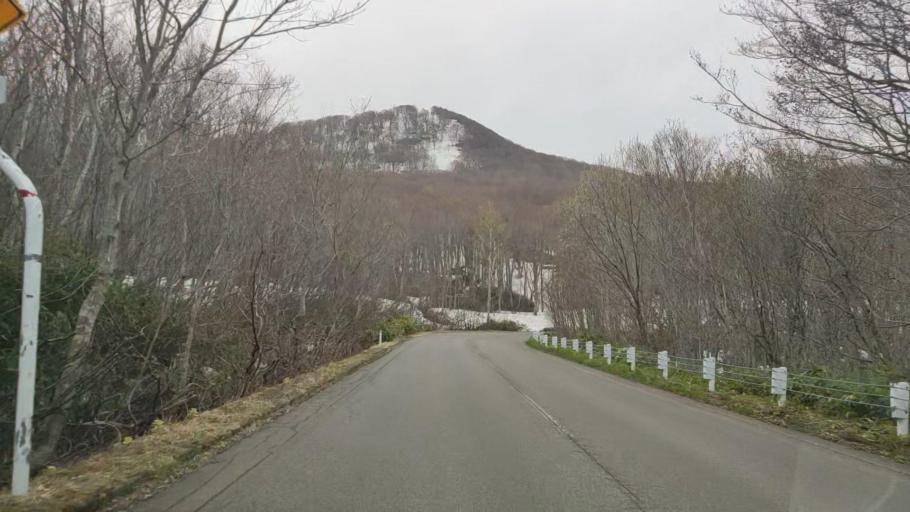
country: JP
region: Aomori
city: Aomori Shi
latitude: 40.6547
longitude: 140.9551
